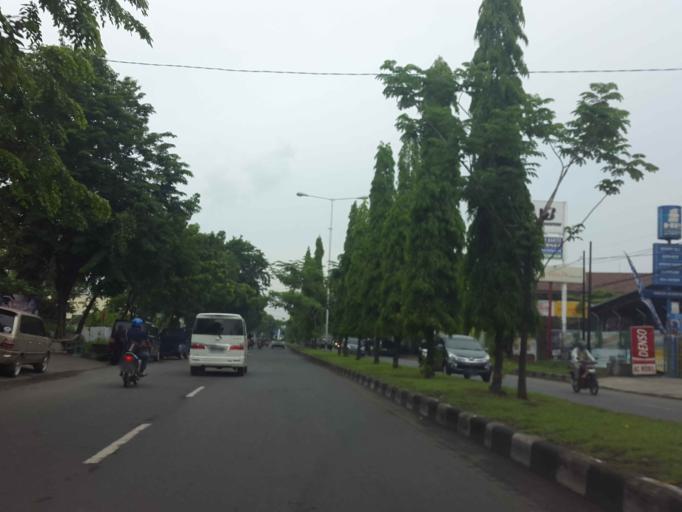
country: ID
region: Central Java
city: Semarang
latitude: -6.9880
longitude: 110.4558
